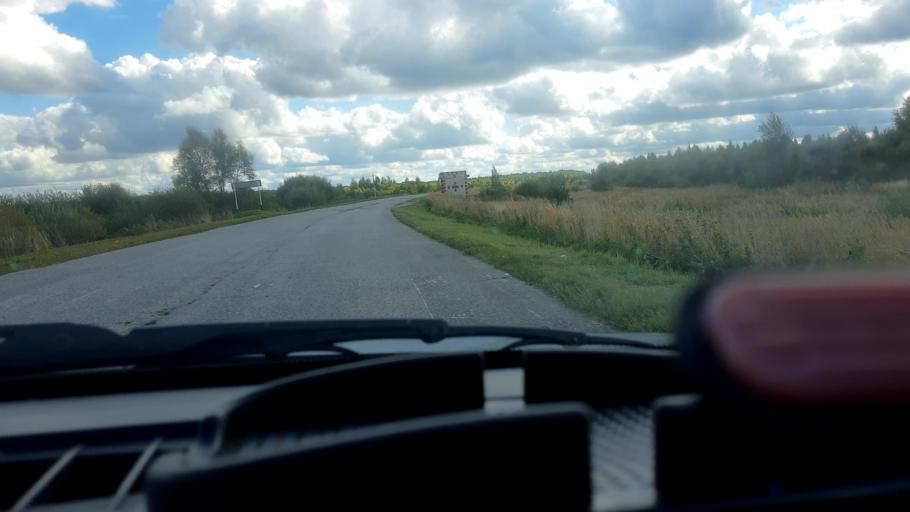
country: RU
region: Mariy-El
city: Kilemary
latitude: 56.9414
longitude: 46.6862
